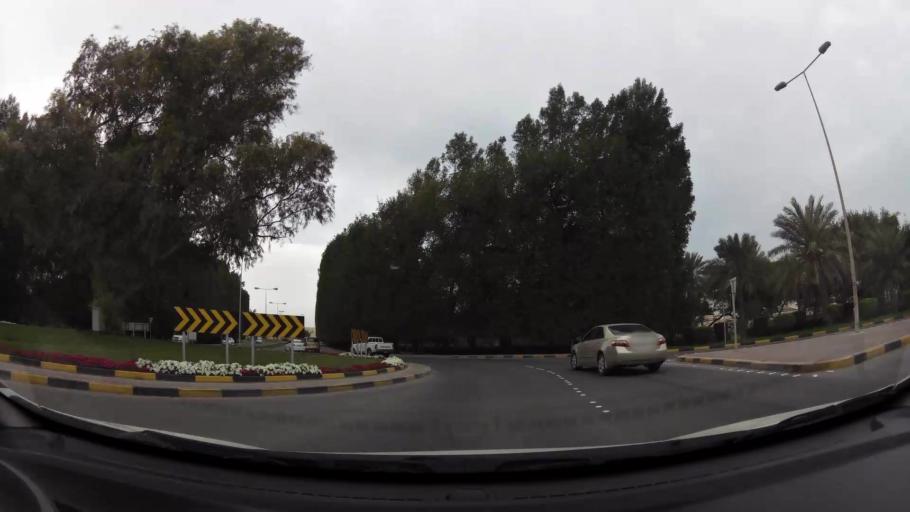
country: BH
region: Northern
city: Ar Rifa'
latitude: 26.1257
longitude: 50.5362
